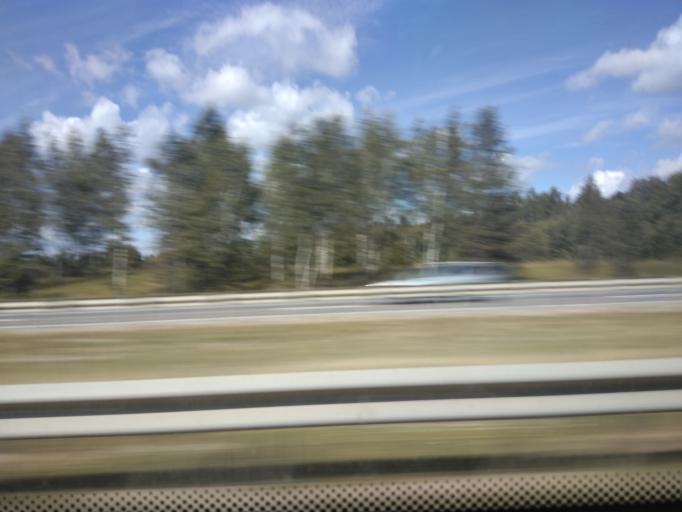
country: RU
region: Tula
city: Zaokskiy
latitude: 54.6500
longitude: 37.5015
